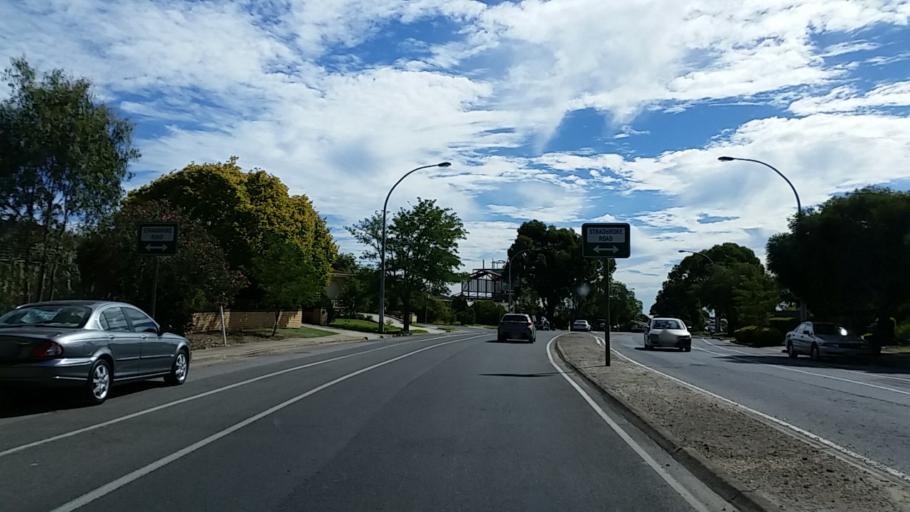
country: AU
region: South Australia
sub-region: Campbelltown
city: Athelstone
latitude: -34.8771
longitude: 138.6934
